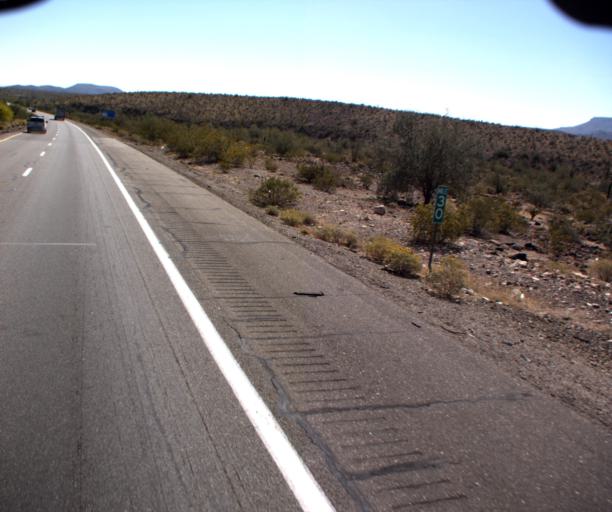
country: US
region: Arizona
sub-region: La Paz County
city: Quartzsite
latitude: 33.6643
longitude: -114.0309
